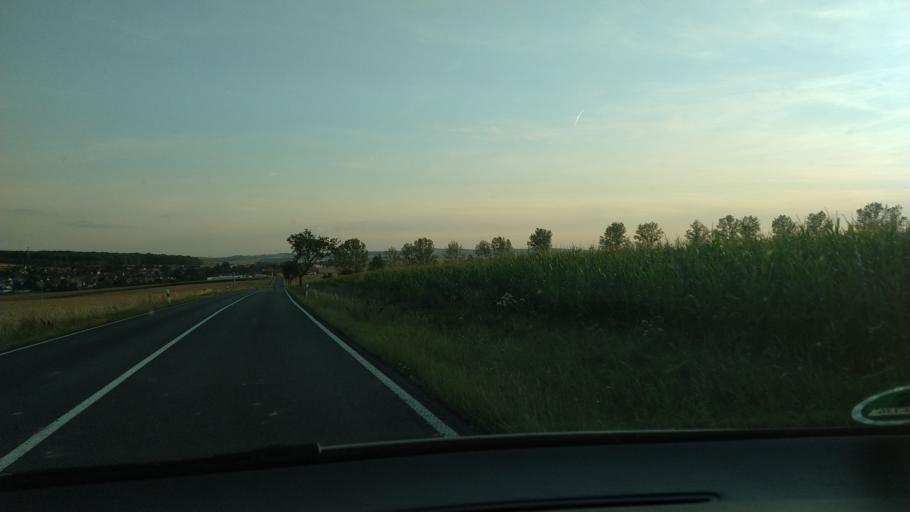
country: DE
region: Thuringia
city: Grossschwabhausen
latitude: 50.9490
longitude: 11.4997
